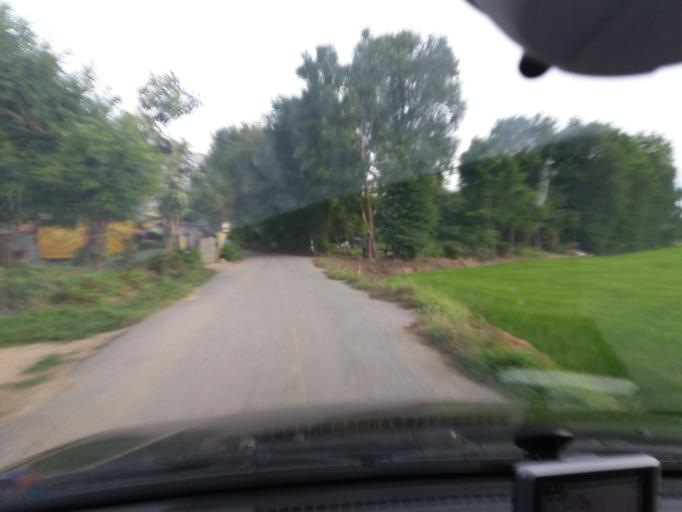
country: TH
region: Suphan Buri
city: Doembang Nangbuat
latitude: 14.8155
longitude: 100.1384
